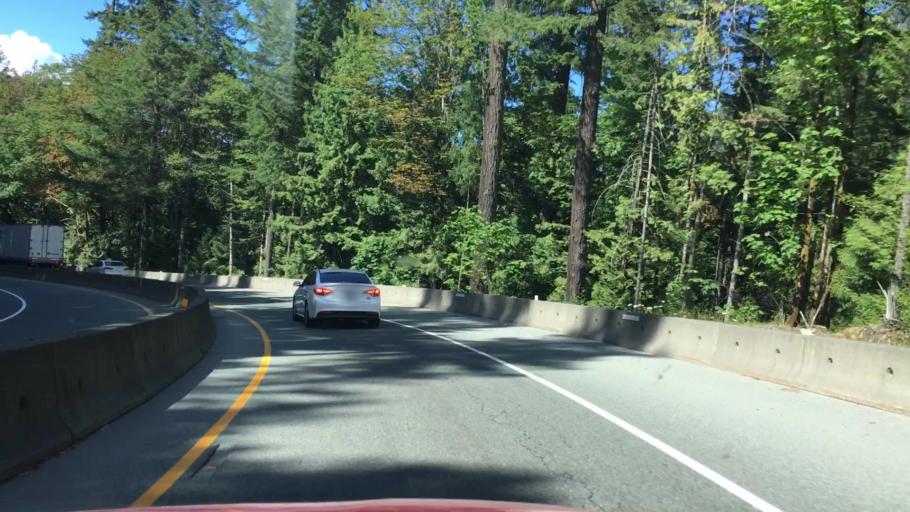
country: CA
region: British Columbia
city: Port Alberni
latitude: 49.2509
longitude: -124.6603
